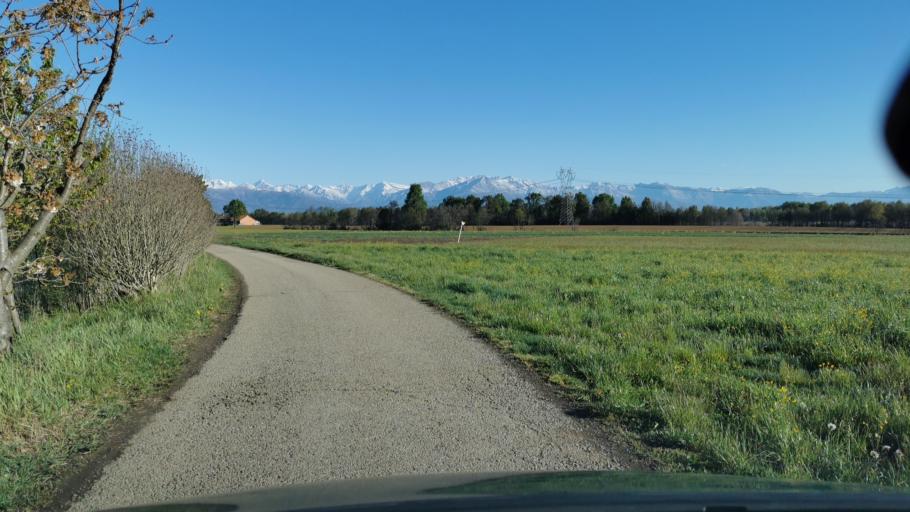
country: IT
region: Piedmont
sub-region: Provincia di Torino
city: Rivarossa
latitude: 45.2202
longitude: 7.7056
